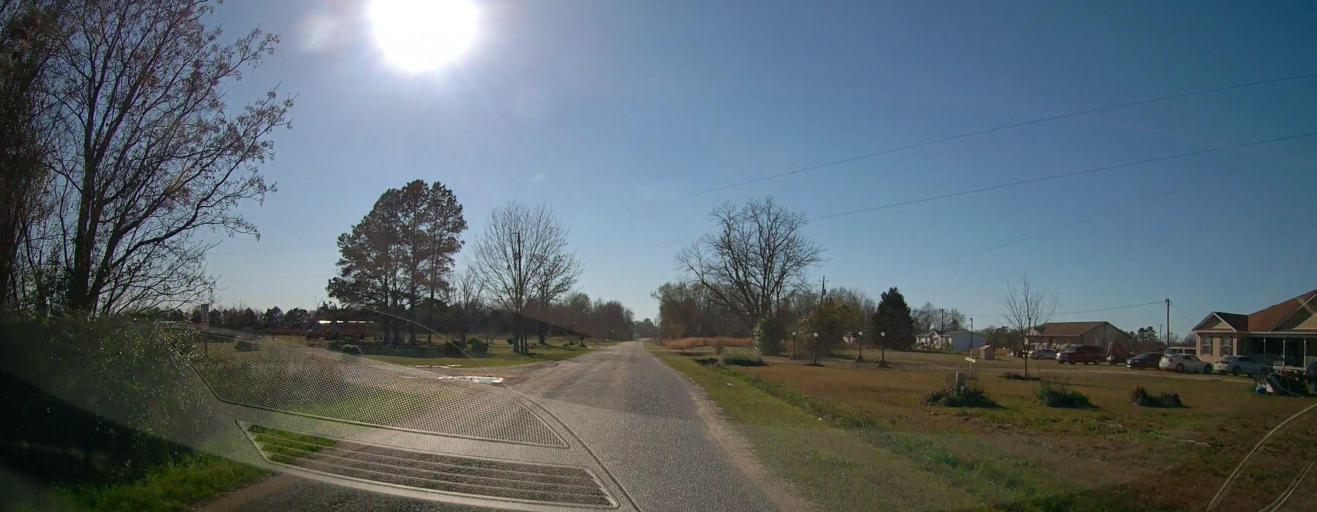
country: US
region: Georgia
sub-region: Taylor County
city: Reynolds
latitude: 32.5550
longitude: -84.0774
